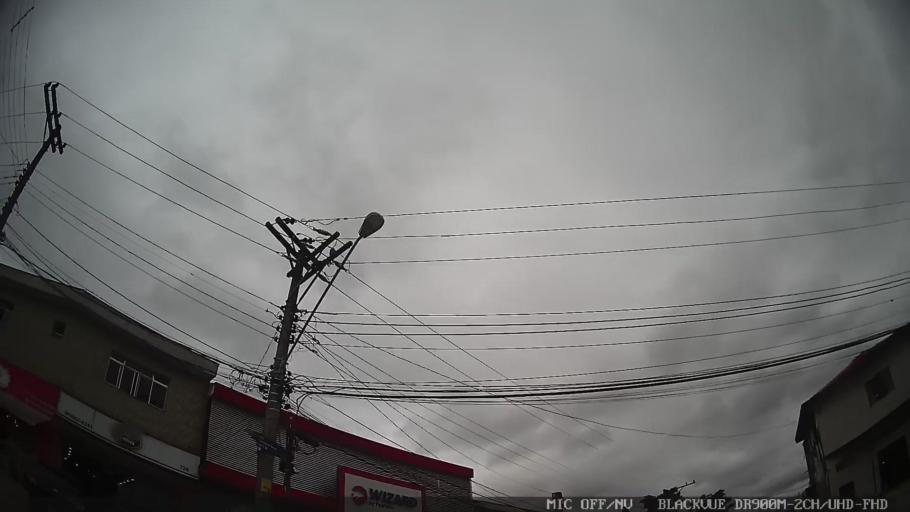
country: BR
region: Sao Paulo
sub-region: Osasco
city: Osasco
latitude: -23.5015
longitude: -46.7388
